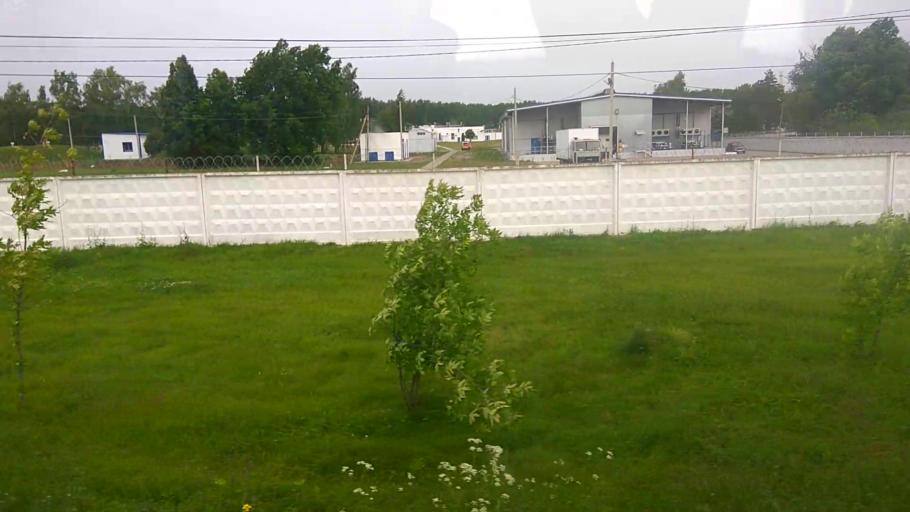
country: RU
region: Moskovskaya
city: Lukhovitsy
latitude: 54.9254
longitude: 38.9977
